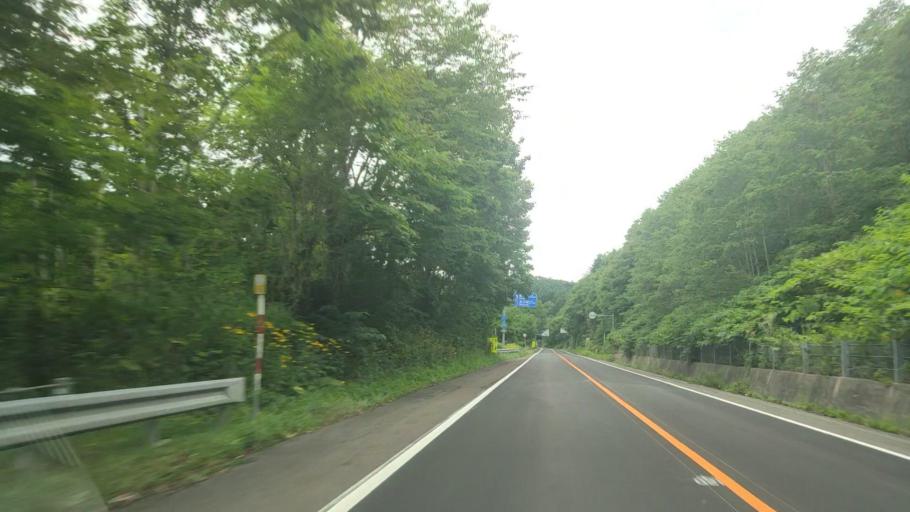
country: JP
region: Hokkaido
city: Niseko Town
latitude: 42.5984
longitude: 140.6054
